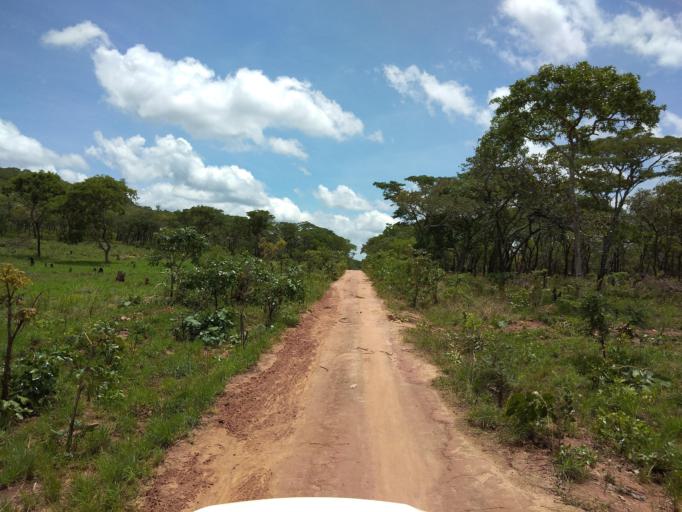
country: ZM
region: Central
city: Mkushi
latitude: -13.9225
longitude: 29.8650
